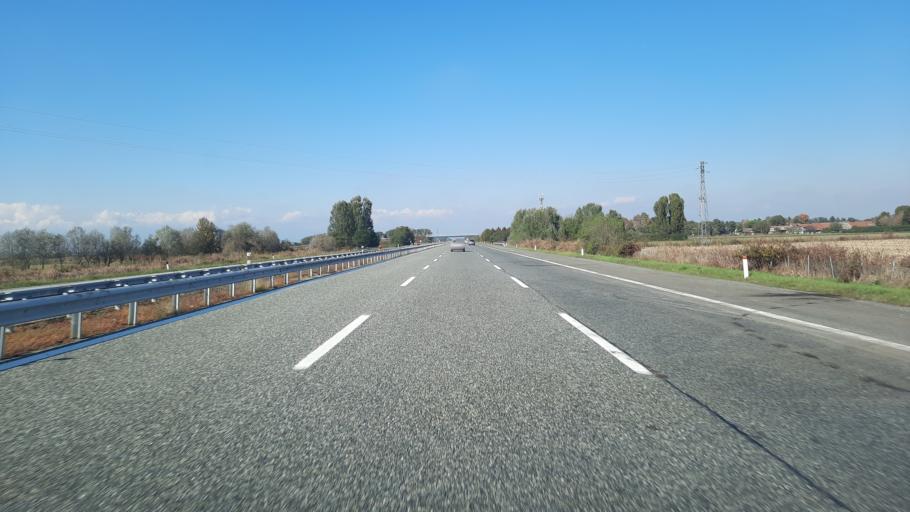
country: IT
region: Piedmont
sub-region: Provincia di Novara
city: Casalbeltrame
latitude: 45.4306
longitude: 8.4628
